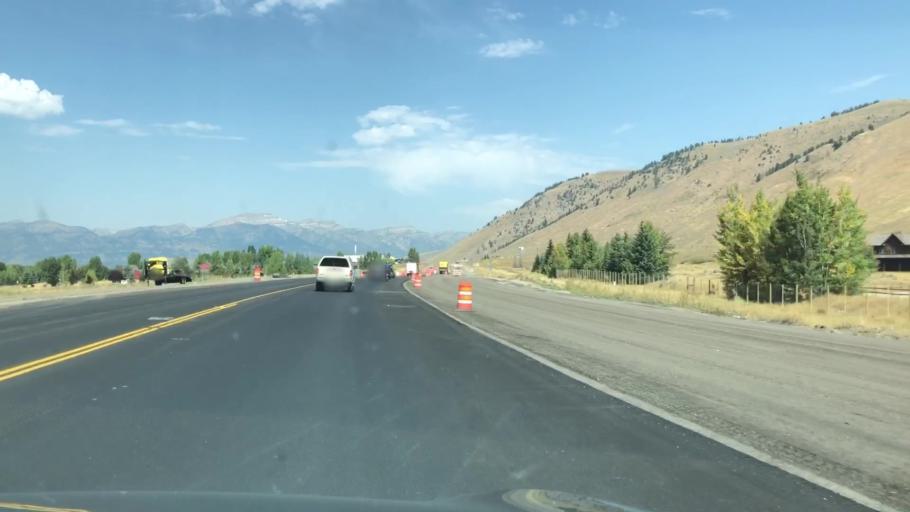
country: US
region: Wyoming
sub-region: Teton County
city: South Park
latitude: 43.4128
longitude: -110.7722
